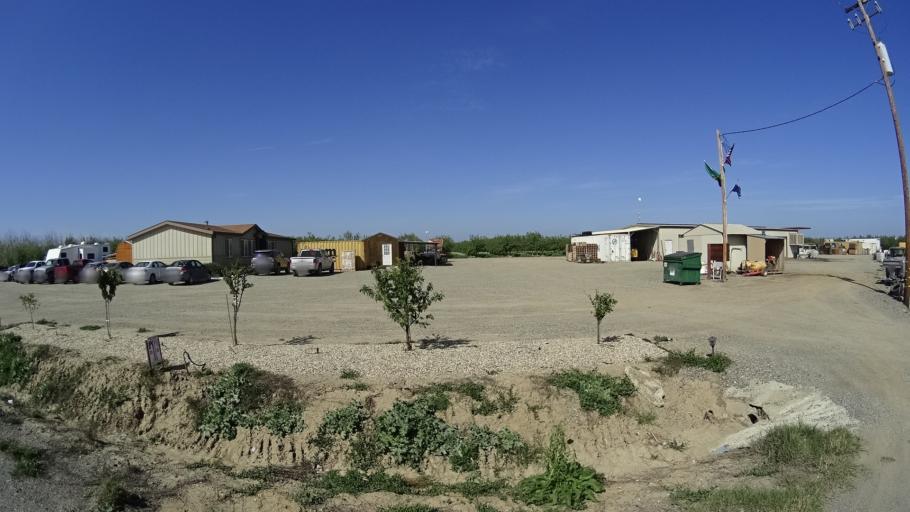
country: US
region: California
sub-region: Glenn County
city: Hamilton City
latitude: 39.6387
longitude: -122.0181
